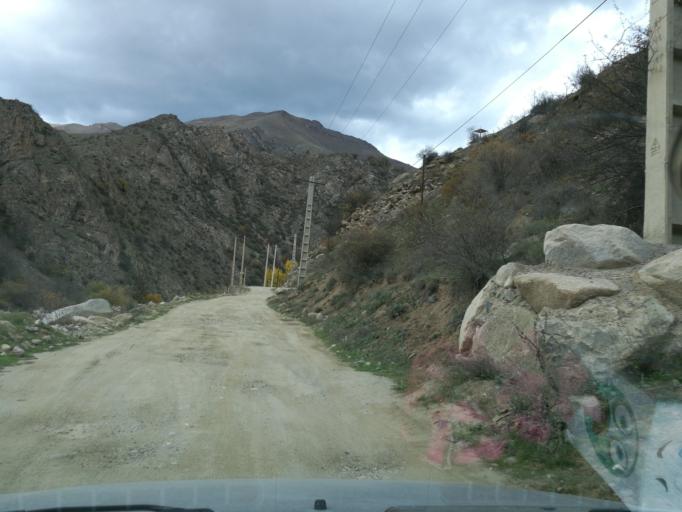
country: IR
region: Mazandaran
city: `Abbasabad
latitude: 36.4361
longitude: 51.0604
